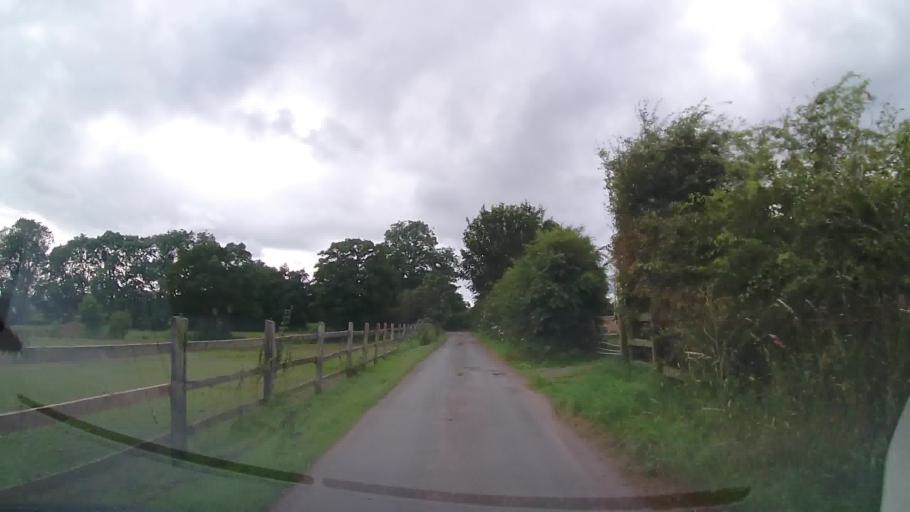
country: GB
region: England
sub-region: Shropshire
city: Prees
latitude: 52.9175
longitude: -2.6852
